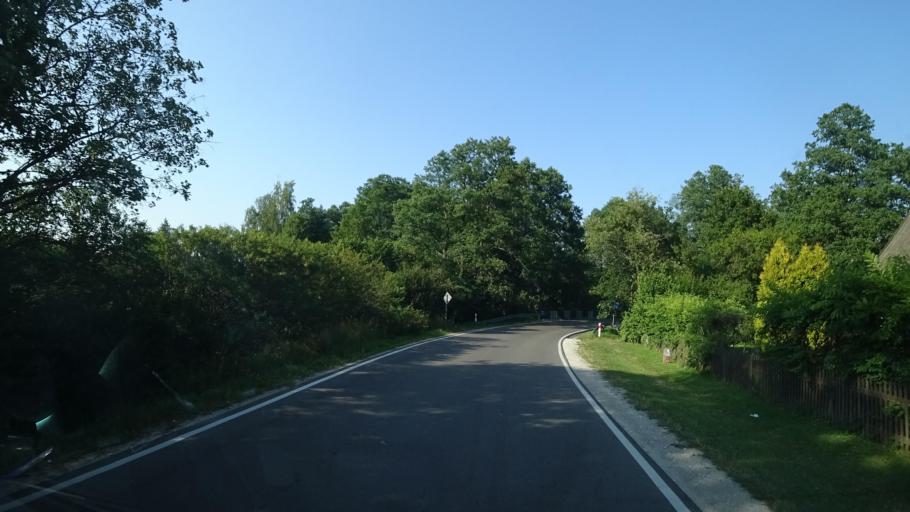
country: PL
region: Pomeranian Voivodeship
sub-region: Powiat bytowski
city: Lipnica
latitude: 53.8312
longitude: 17.4478
